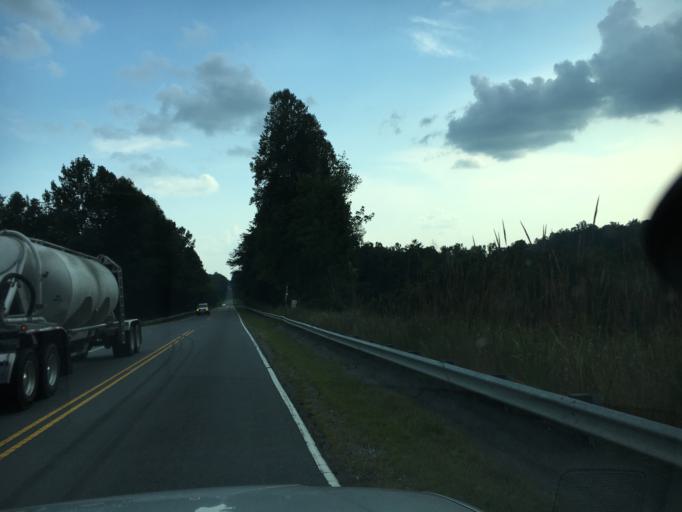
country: US
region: North Carolina
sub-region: Rutherford County
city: Rutherfordton
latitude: 35.4917
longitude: -81.9792
